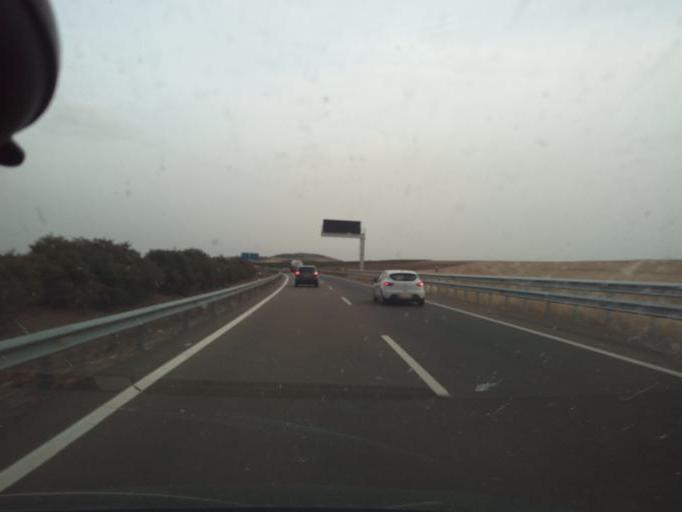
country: ES
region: Extremadura
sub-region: Provincia de Badajoz
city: Merida
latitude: 38.9472
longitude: -6.3195
